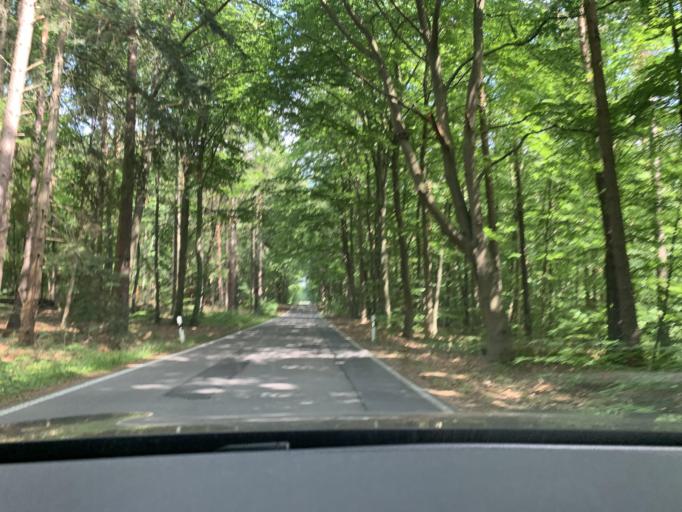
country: DE
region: Brandenburg
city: Rheinsberg
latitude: 53.1841
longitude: 12.8181
